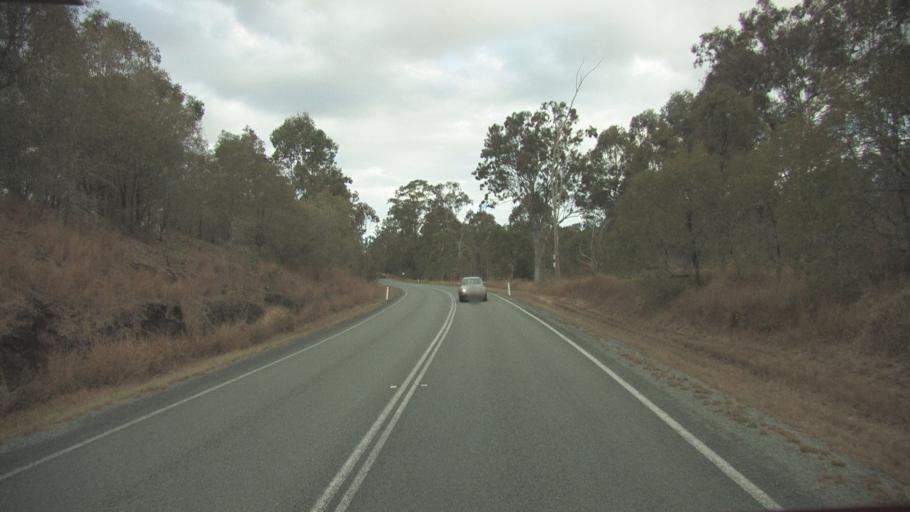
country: AU
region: Queensland
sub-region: Logan
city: Cedar Vale
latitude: -27.8962
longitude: 153.0881
